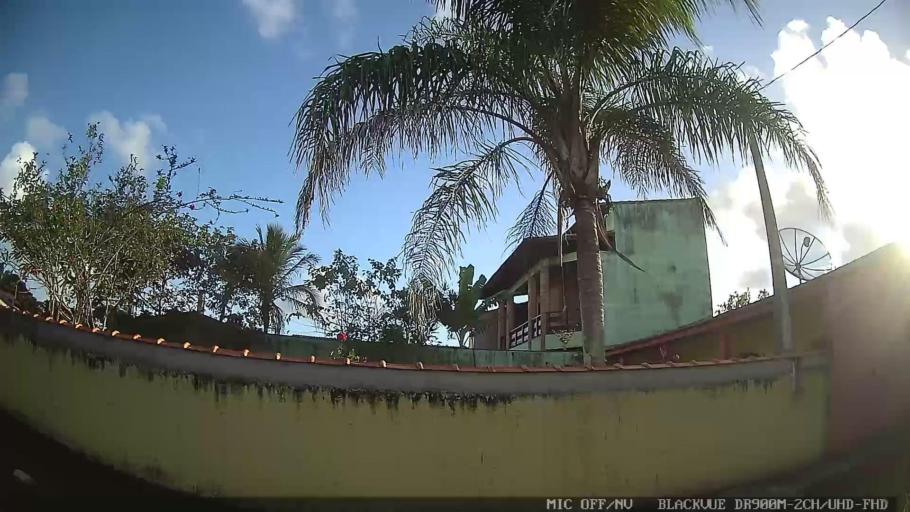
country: BR
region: Sao Paulo
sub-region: Itanhaem
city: Itanhaem
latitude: -24.1403
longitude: -46.7194
